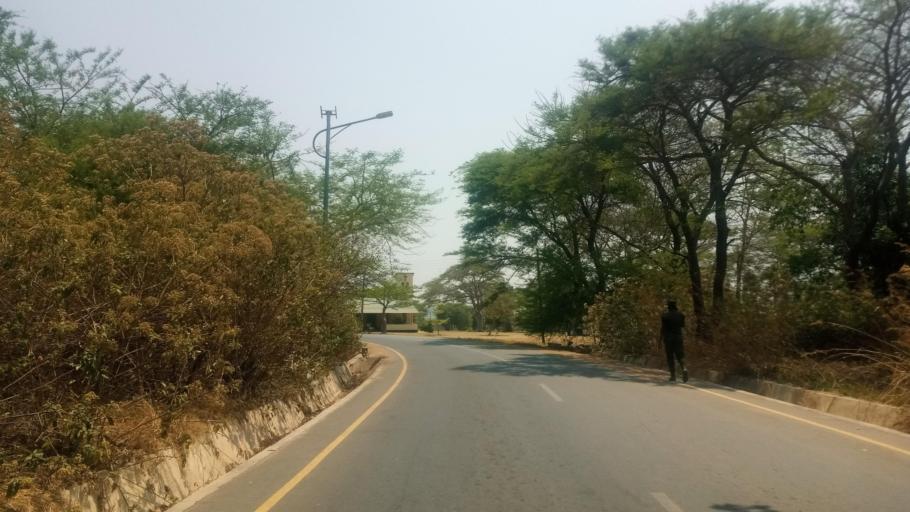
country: ZM
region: Lusaka
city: Lusaka
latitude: -15.4546
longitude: 28.4406
